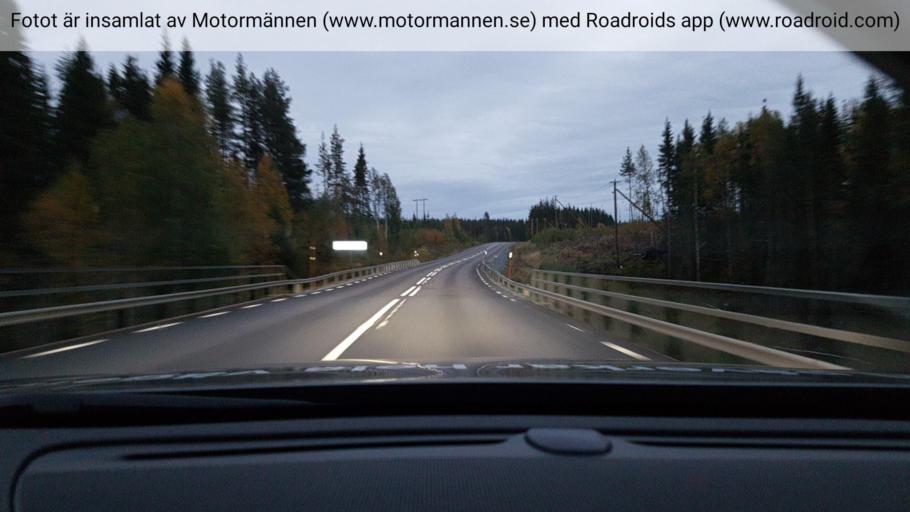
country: SE
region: Norrbotten
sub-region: Alvsbyns Kommun
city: AElvsbyn
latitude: 65.7452
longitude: 20.9414
